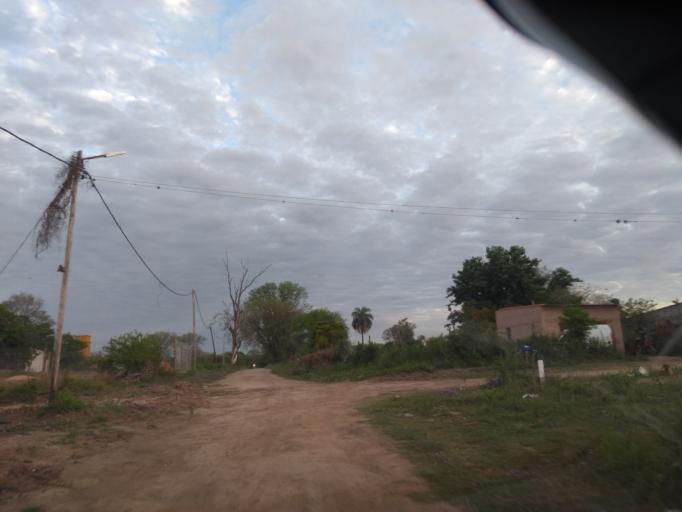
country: AR
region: Chaco
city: Fontana
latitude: -27.4088
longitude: -59.0502
